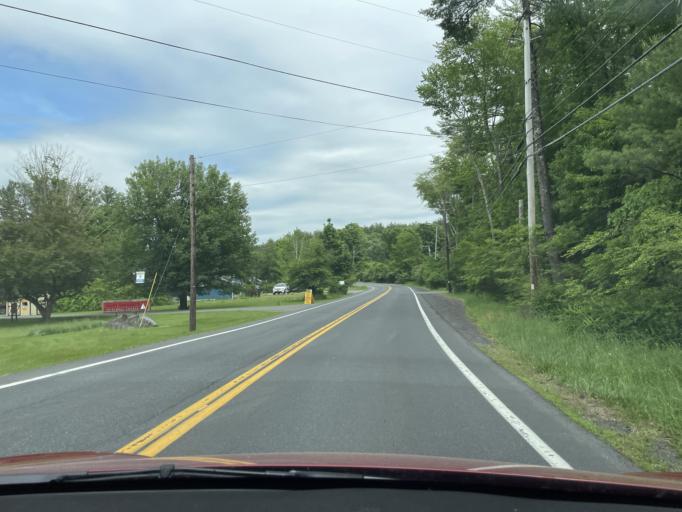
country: US
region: New York
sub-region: Ulster County
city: Woodstock
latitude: 42.0370
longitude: -74.1037
